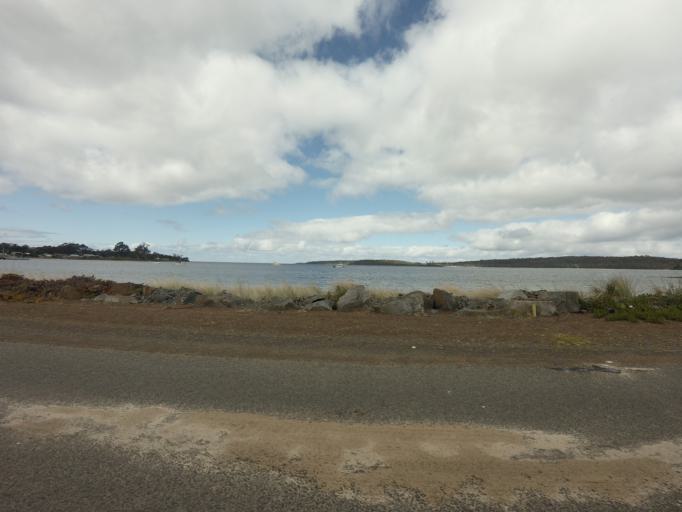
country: AU
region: Tasmania
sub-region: Huon Valley
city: Geeveston
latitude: -43.4323
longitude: 146.9702
